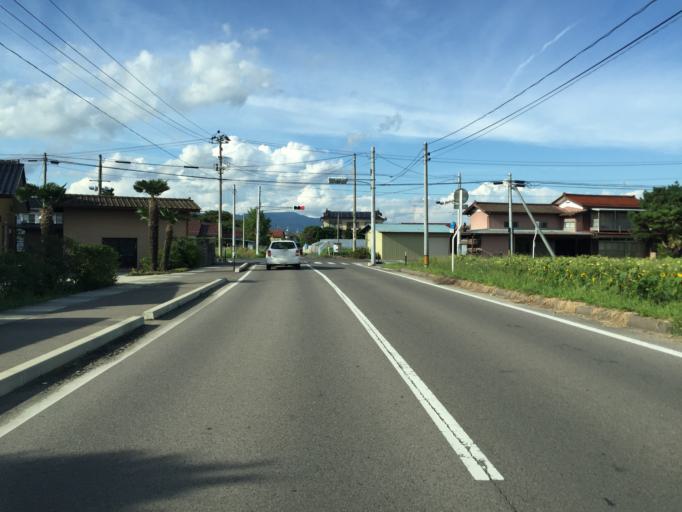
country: JP
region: Fukushima
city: Hobaramachi
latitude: 37.8206
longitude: 140.5717
